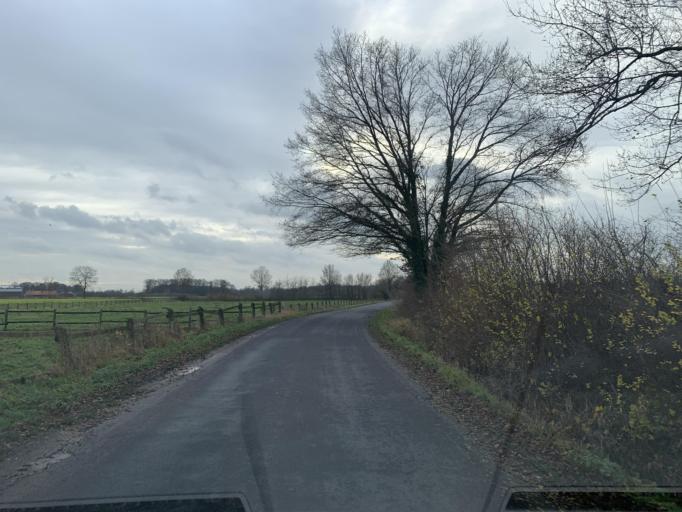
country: DE
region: North Rhine-Westphalia
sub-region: Regierungsbezirk Munster
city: Ascheberg
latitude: 51.8069
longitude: 7.6334
